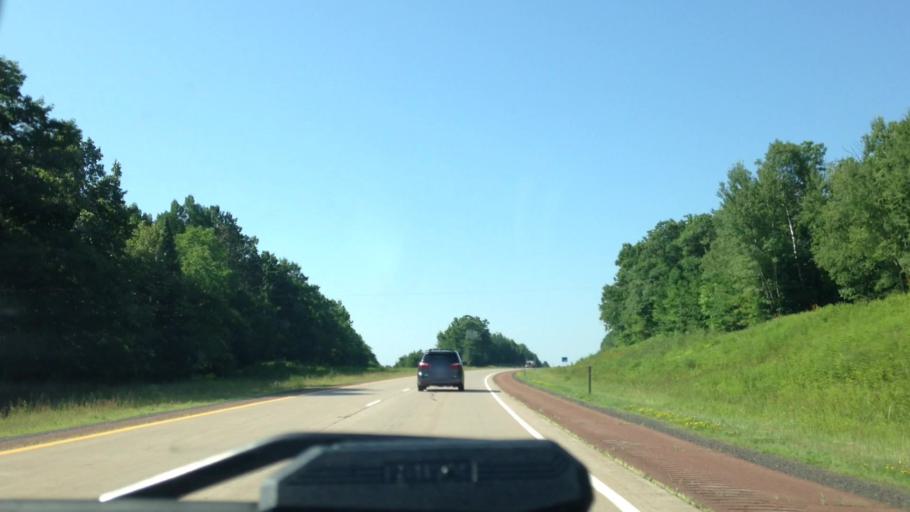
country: US
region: Wisconsin
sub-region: Douglas County
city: Lake Nebagamon
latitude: 46.3899
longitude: -91.8193
